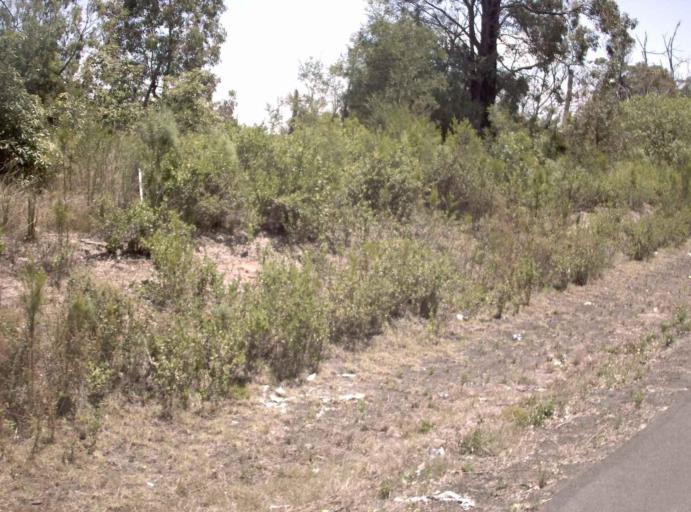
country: AU
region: Victoria
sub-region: East Gippsland
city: Lakes Entrance
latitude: -37.8459
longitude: 148.0411
